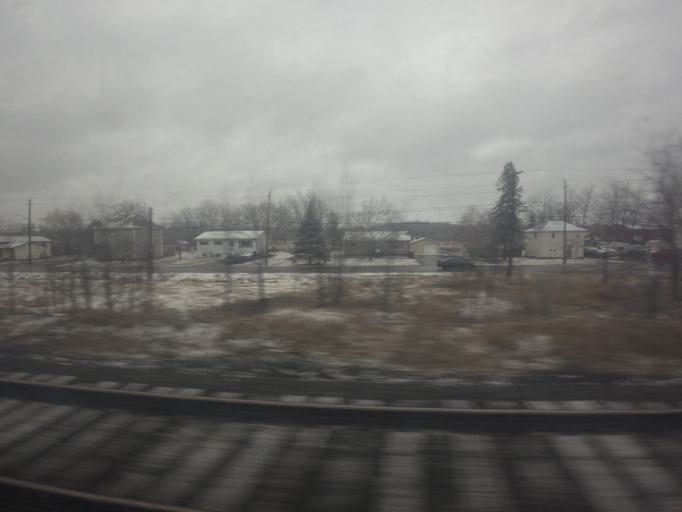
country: US
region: New York
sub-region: Jefferson County
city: Alexandria Bay
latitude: 44.4045
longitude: -76.0159
